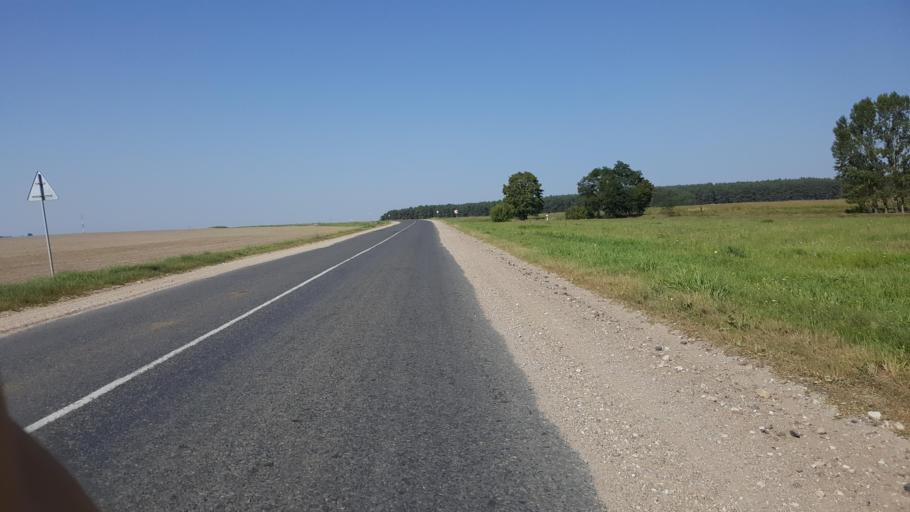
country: BY
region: Brest
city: Kamyanyets
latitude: 52.4175
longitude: 23.6596
